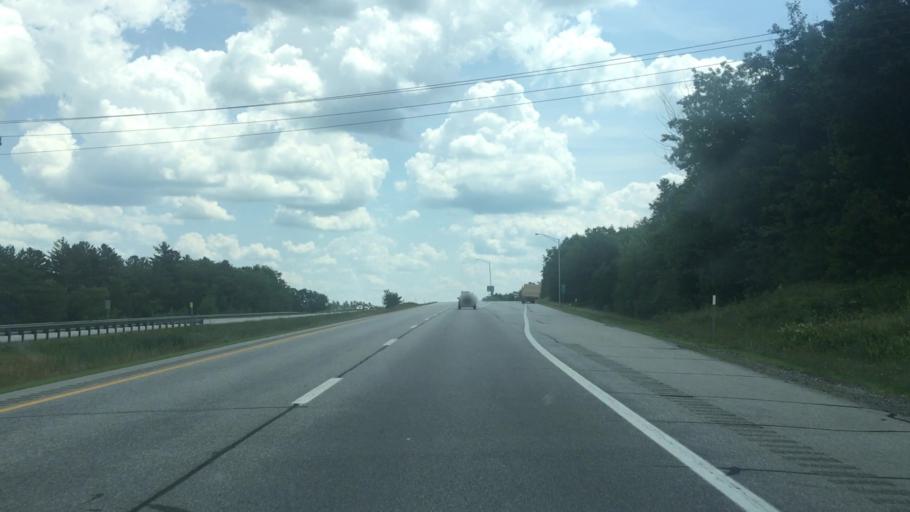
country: US
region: New Hampshire
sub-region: Merrimack County
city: New London
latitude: 43.4272
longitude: -72.0398
